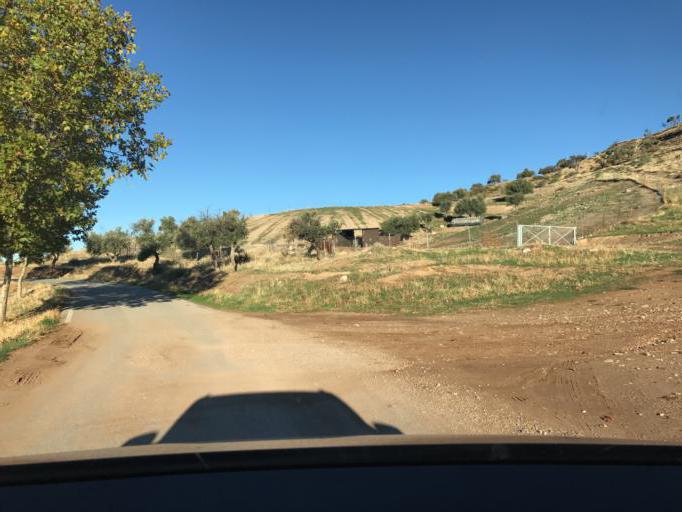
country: ES
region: Andalusia
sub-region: Provincia de Granada
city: Viznar
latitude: 37.2411
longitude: -3.5486
